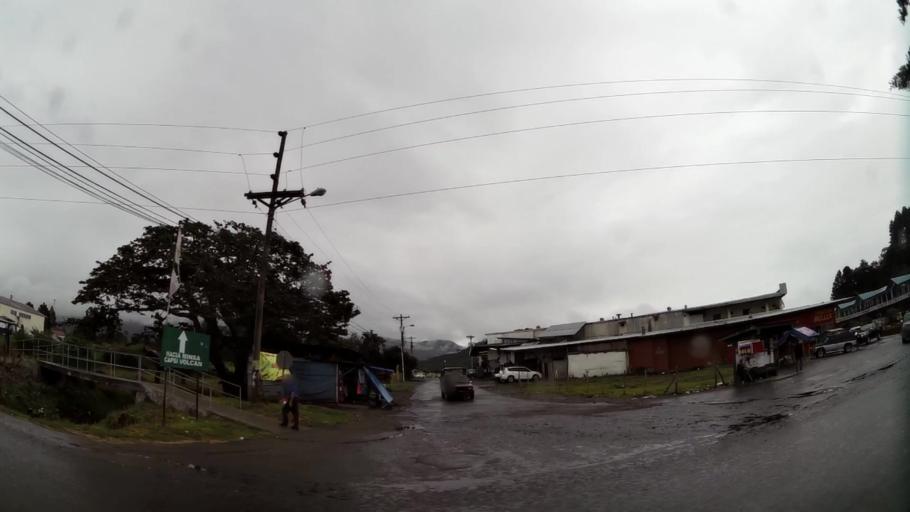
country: PA
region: Chiriqui
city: Volcan
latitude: 8.7764
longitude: -82.6401
